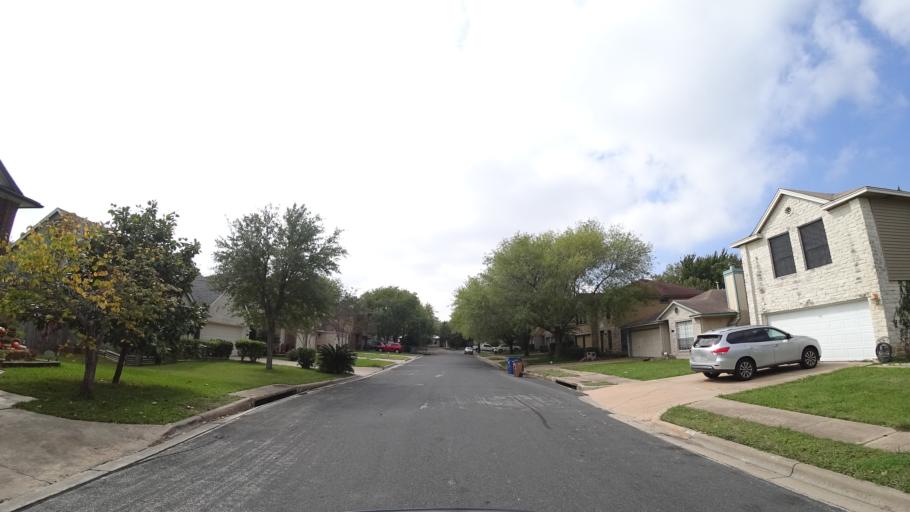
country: US
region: Texas
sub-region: Travis County
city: Shady Hollow
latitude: 30.1939
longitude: -97.8345
